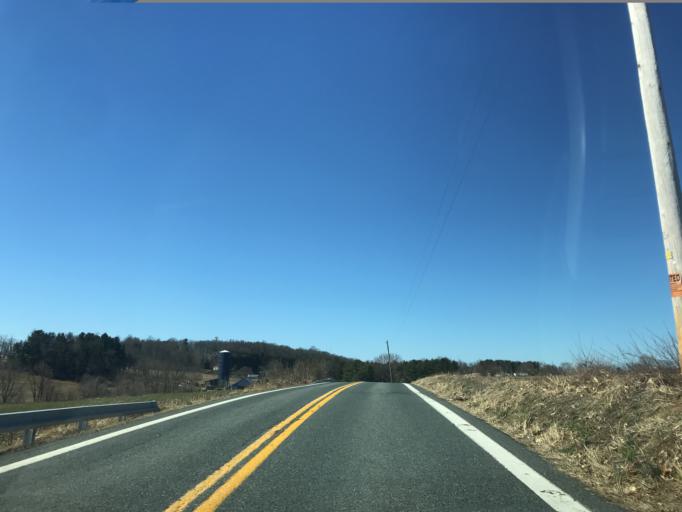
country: US
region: Pennsylvania
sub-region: York County
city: Susquehanna Trails
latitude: 39.7008
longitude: -76.4123
